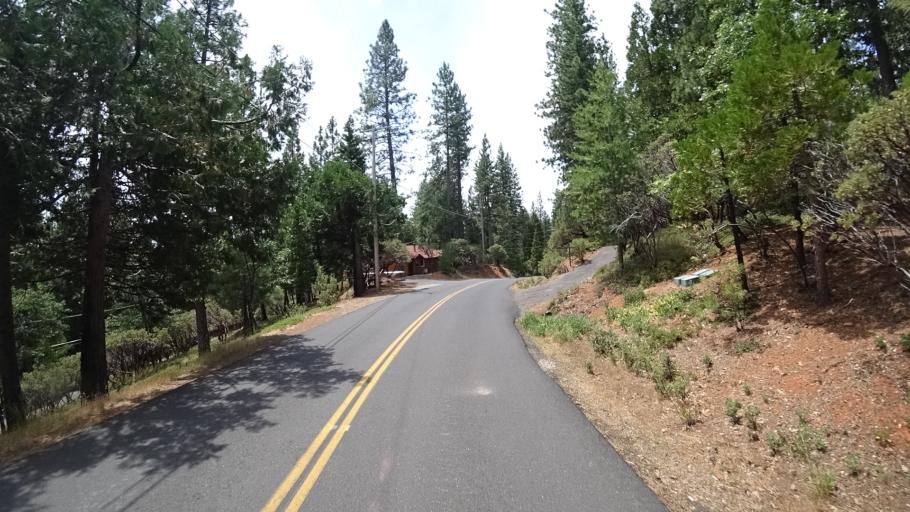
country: US
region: California
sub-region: Calaveras County
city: Arnold
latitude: 38.2450
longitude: -120.3497
